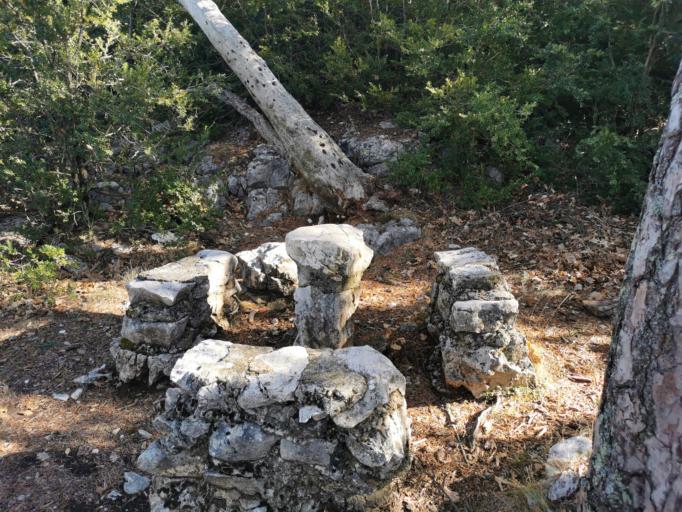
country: FR
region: Provence-Alpes-Cote d'Azur
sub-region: Departement des Alpes-de-Haute-Provence
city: Castellane
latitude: 43.7655
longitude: 6.3687
